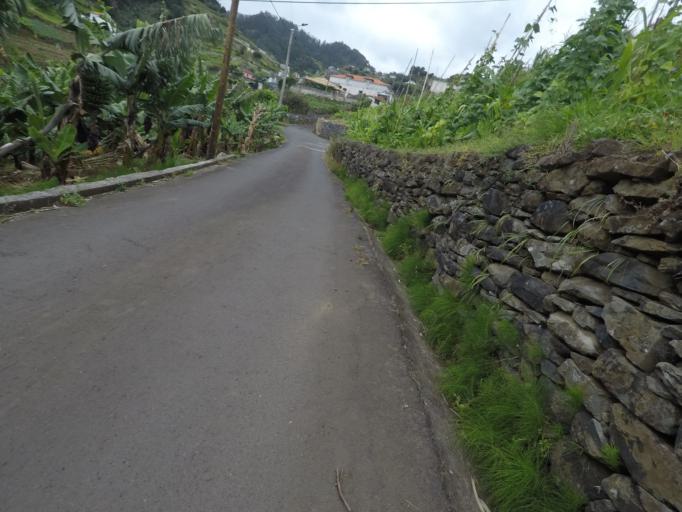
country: PT
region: Madeira
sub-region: Santana
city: Santana
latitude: 32.7713
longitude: -16.8362
